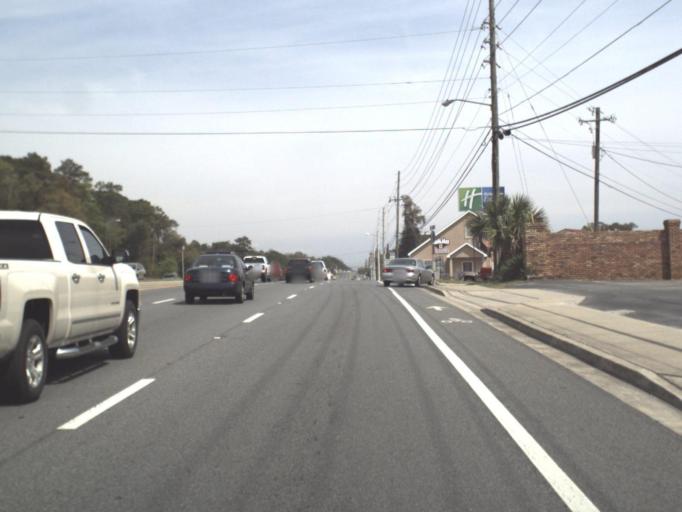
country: US
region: Florida
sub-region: Okaloosa County
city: Niceville
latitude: 30.5218
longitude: -86.4923
